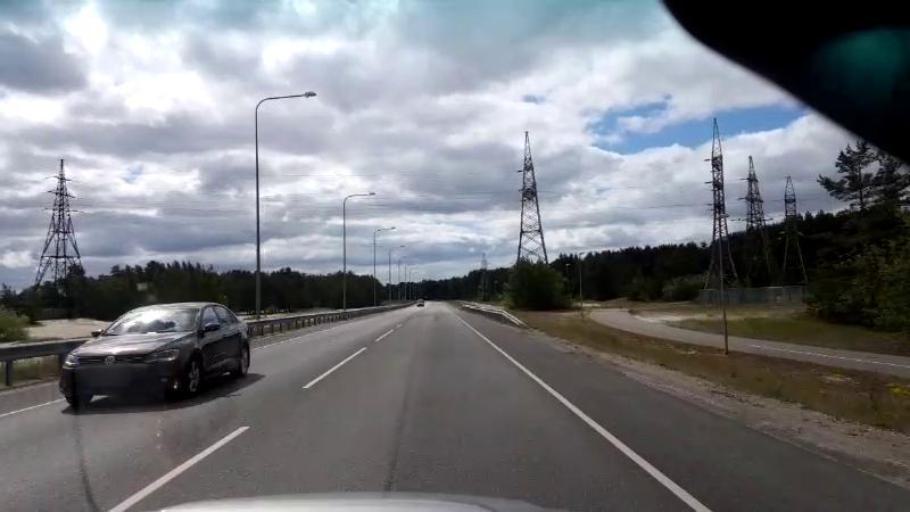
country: EE
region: Paernumaa
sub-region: Paernu linn
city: Parnu
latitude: 58.3677
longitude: 24.5576
